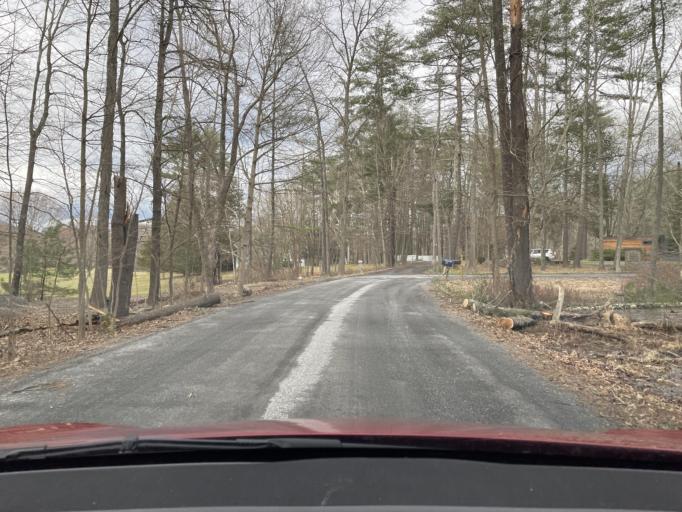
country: US
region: New York
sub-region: Ulster County
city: Woodstock
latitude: 42.0315
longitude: -74.1070
